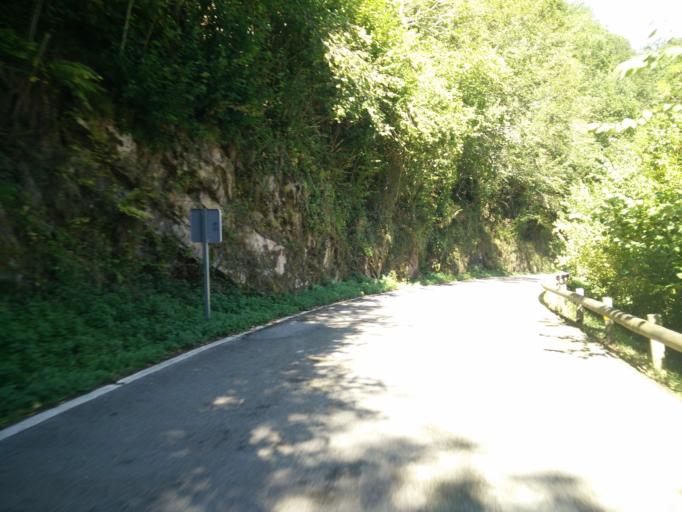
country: ES
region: Cantabria
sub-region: Provincia de Cantabria
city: Ruente
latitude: 43.1106
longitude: -4.2920
